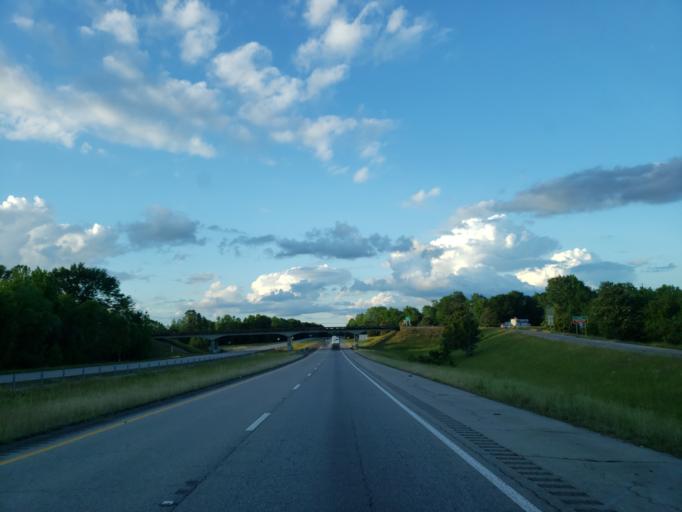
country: US
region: Alabama
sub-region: Sumter County
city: York
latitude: 32.4244
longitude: -88.4529
